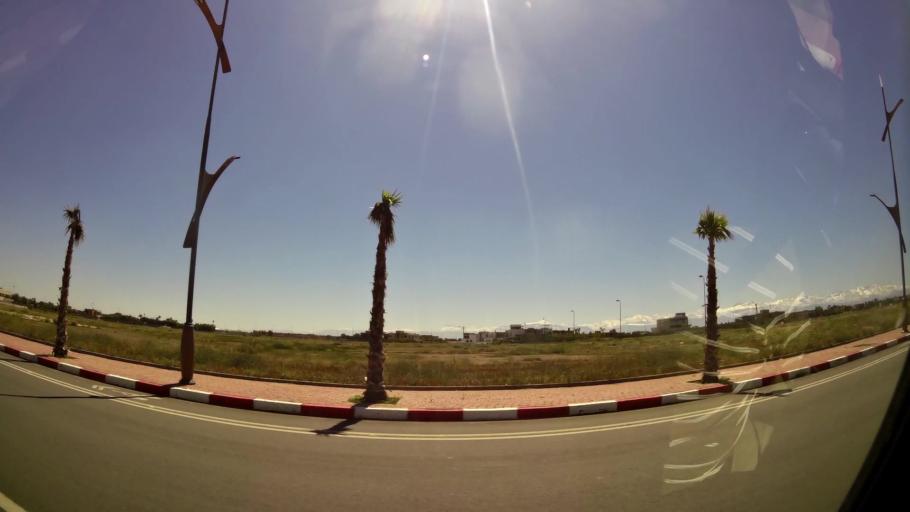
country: MA
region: Marrakech-Tensift-Al Haouz
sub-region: Marrakech
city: Marrakesh
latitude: 31.5963
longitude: -8.0039
